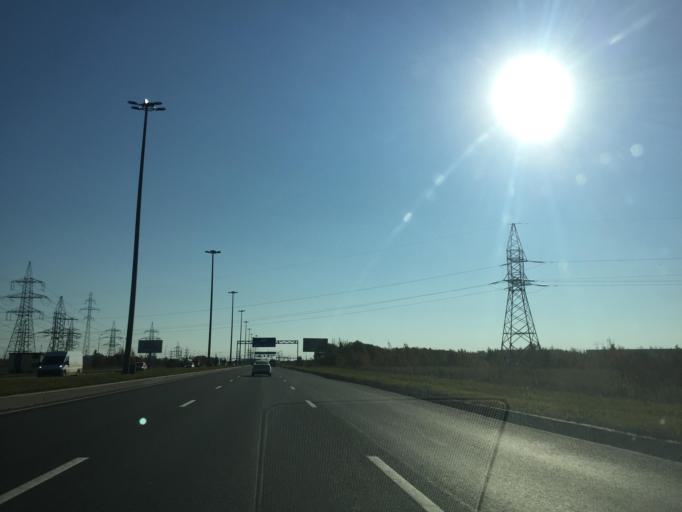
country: RU
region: St.-Petersburg
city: Petro-Slavyanka
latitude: 59.7530
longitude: 30.5238
